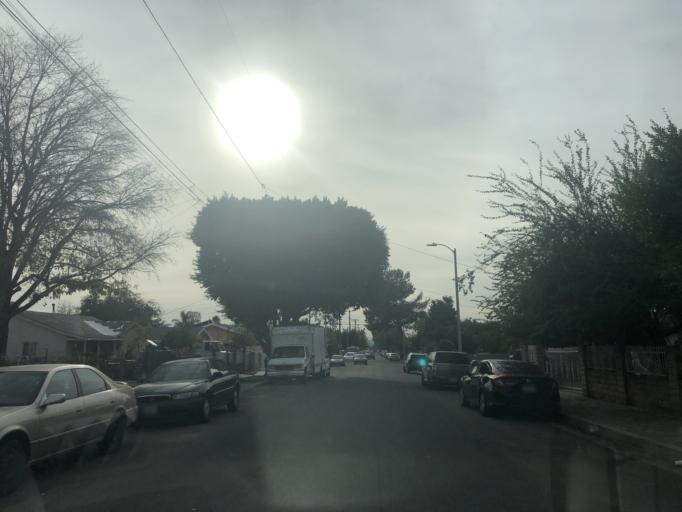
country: US
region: California
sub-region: Los Angeles County
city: San Fernando
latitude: 34.2663
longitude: -118.4327
